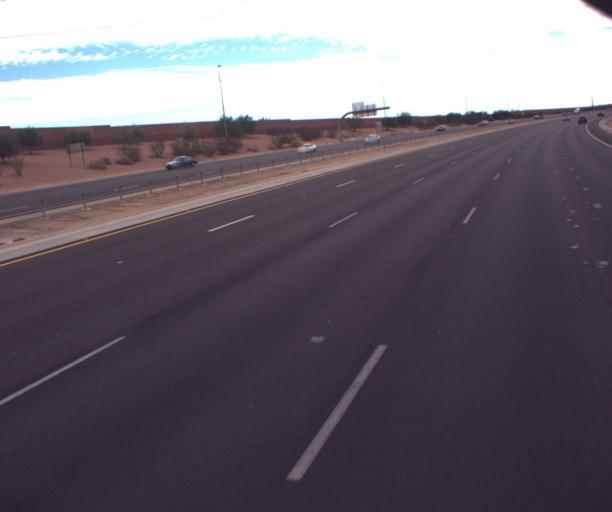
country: US
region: Arizona
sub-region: Pinal County
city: Apache Junction
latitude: 33.4007
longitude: -111.6409
